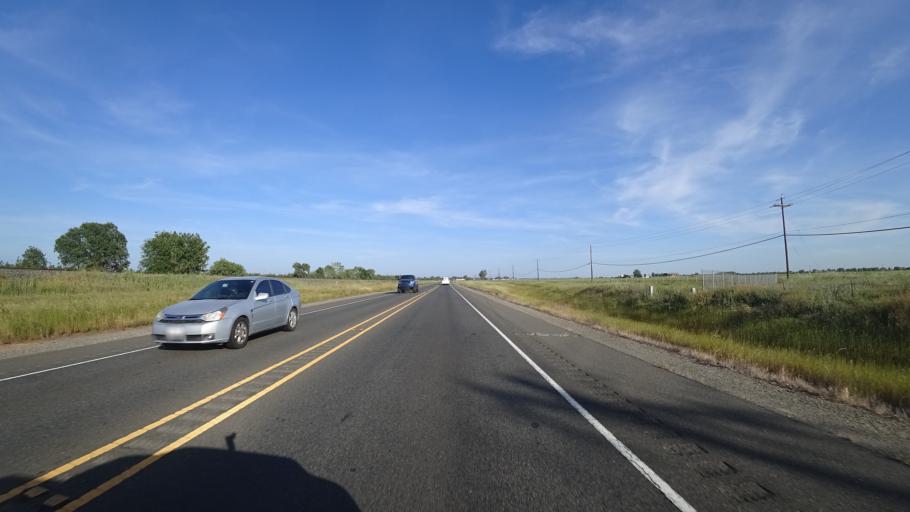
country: US
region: California
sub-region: Placer County
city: Sheridan
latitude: 38.9941
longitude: -121.3965
